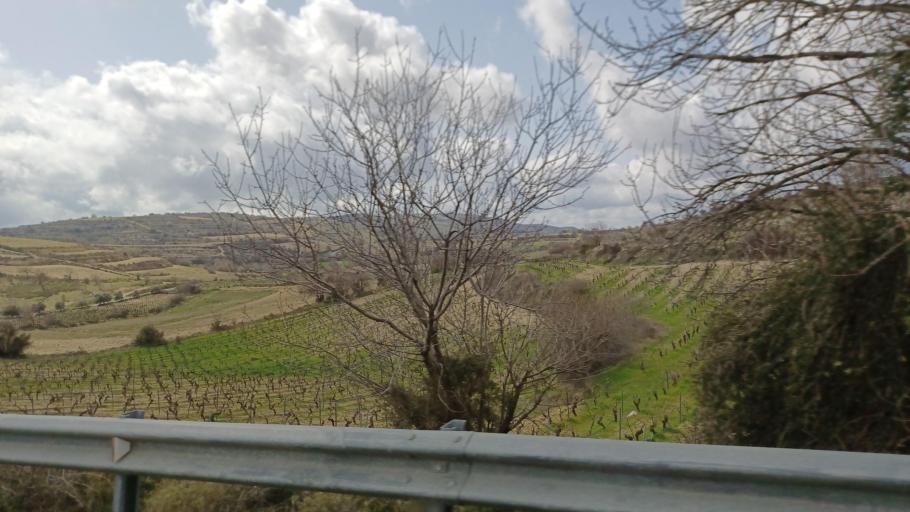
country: CY
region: Limassol
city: Pachna
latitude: 34.8165
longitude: 32.7751
